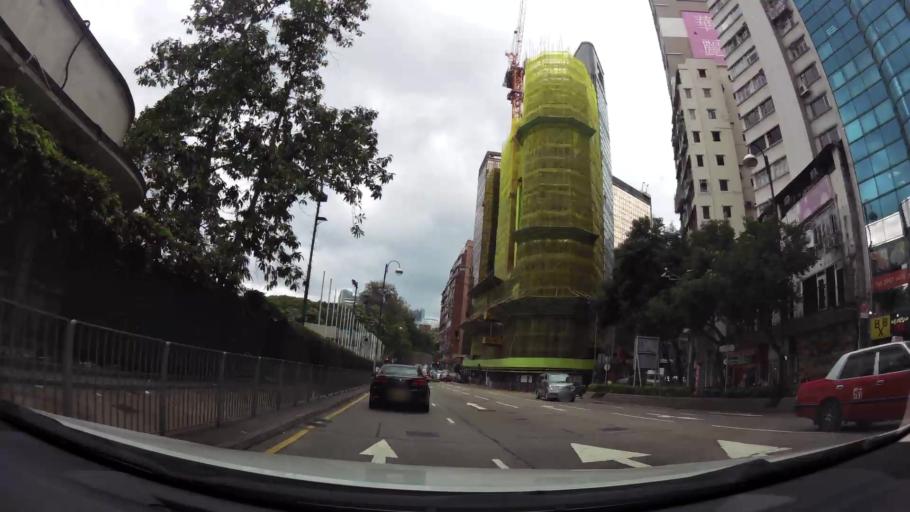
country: HK
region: Kowloon City
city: Kowloon
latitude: 22.3034
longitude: 114.1739
